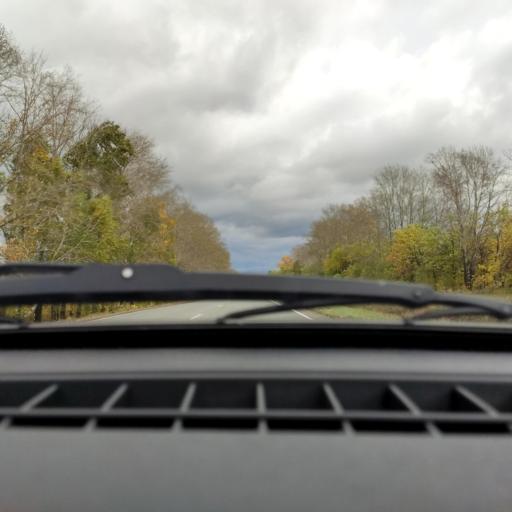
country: RU
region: Bashkortostan
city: Shafranovo
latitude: 54.0143
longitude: 54.8154
